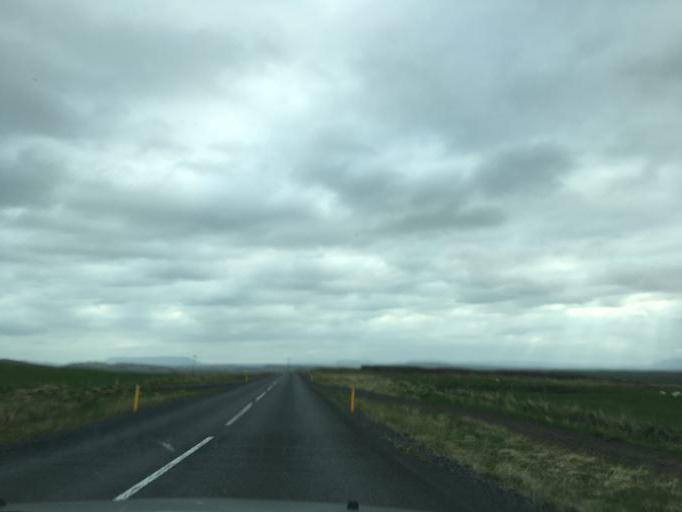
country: IS
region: South
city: Vestmannaeyjar
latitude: 64.2383
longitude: -20.2280
